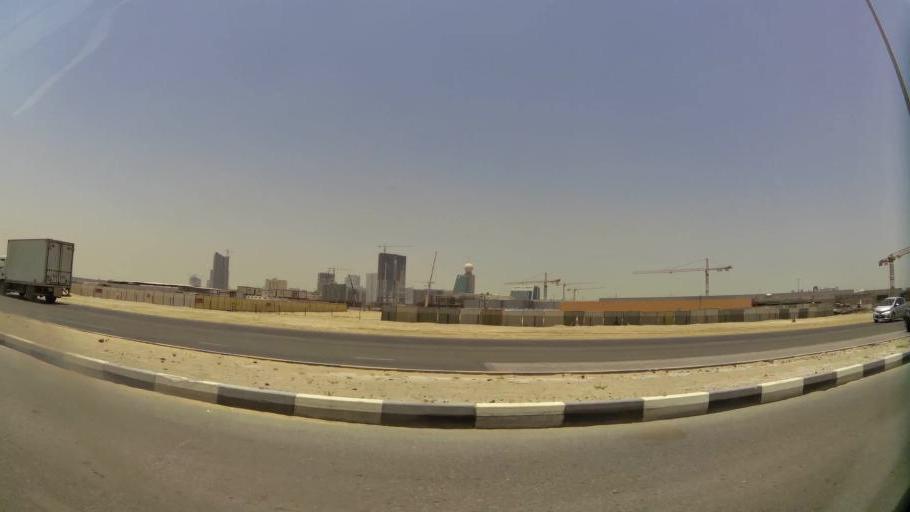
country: AE
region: Ajman
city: Ajman
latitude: 25.3991
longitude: 55.4822
